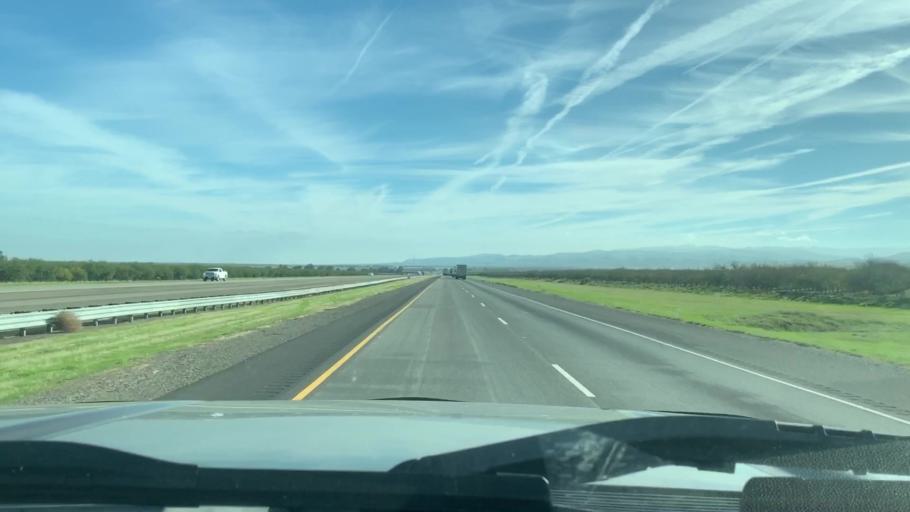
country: US
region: California
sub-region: Fresno County
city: Firebaugh
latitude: 36.6696
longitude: -120.6461
